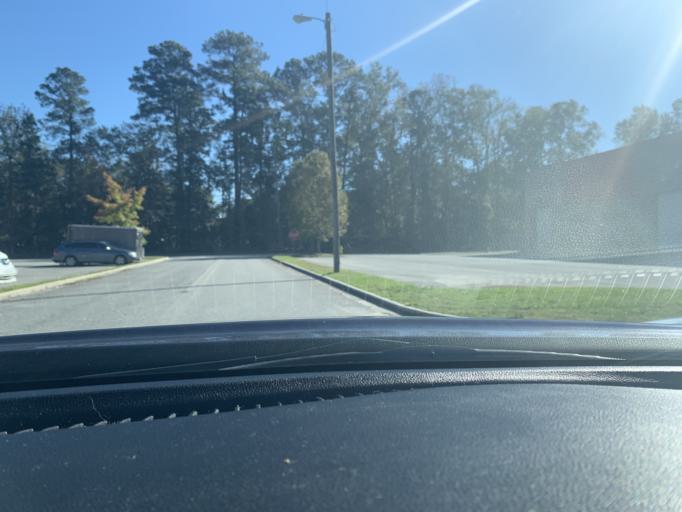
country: US
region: Georgia
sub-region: Chatham County
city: Pooler
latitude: 32.1237
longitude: -81.2635
